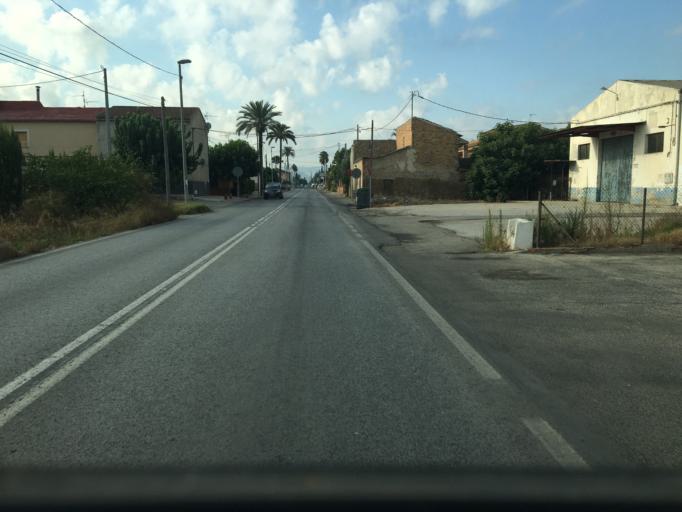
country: ES
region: Murcia
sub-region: Murcia
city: Santomera
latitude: 38.0351
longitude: -1.0441
